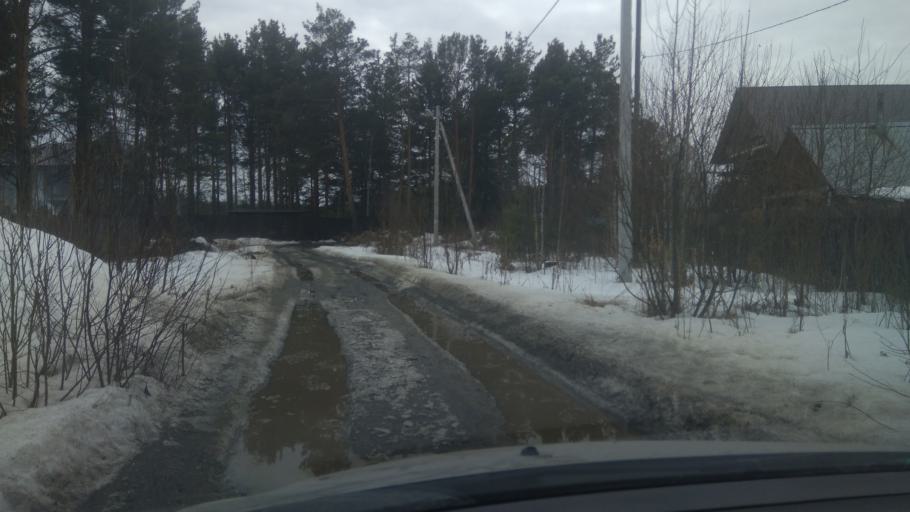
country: RU
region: Sverdlovsk
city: Severka
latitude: 56.8536
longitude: 60.3791
